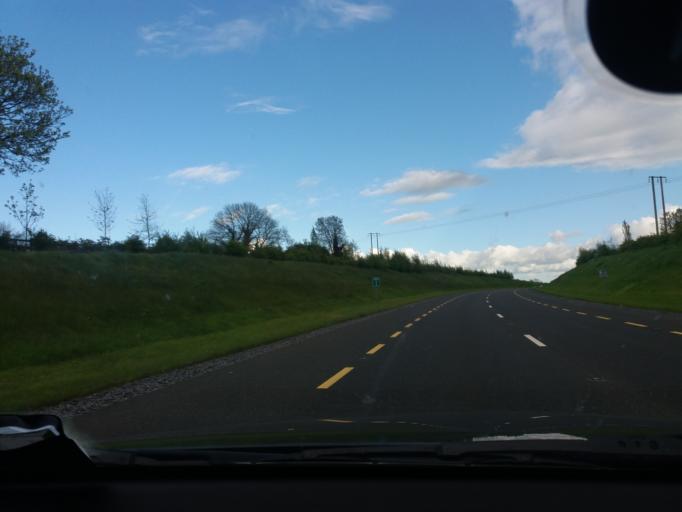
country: IE
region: Leinster
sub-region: Kilkenny
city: Kilkenny
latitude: 52.6568
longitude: -7.2037
